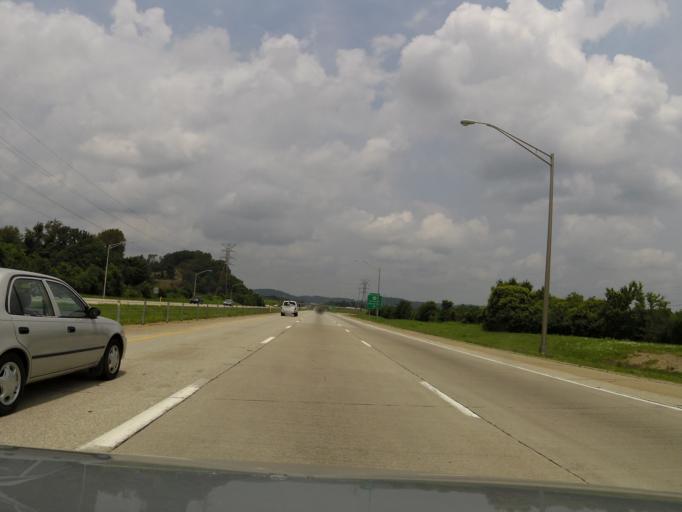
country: US
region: Kentucky
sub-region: Bullitt County
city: Shepherdsville
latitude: 37.9183
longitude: -85.6870
